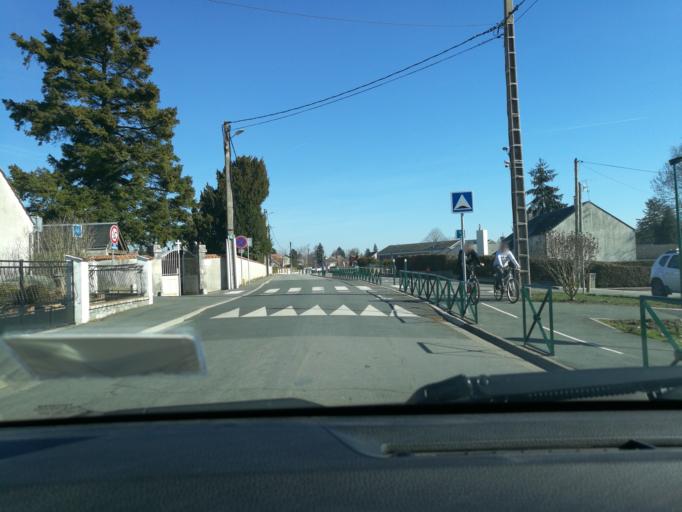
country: FR
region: Centre
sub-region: Departement du Loiret
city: Saint-Ay
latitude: 47.8611
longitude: 1.7536
